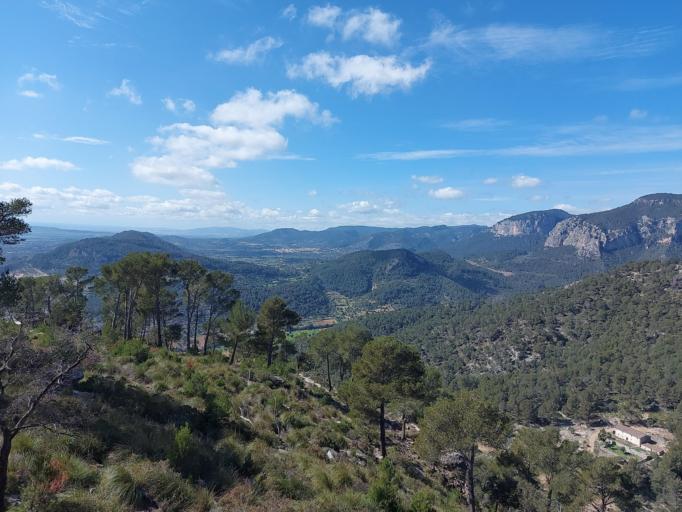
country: ES
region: Balearic Islands
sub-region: Illes Balears
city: Lloseta
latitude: 39.7321
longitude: 2.8560
